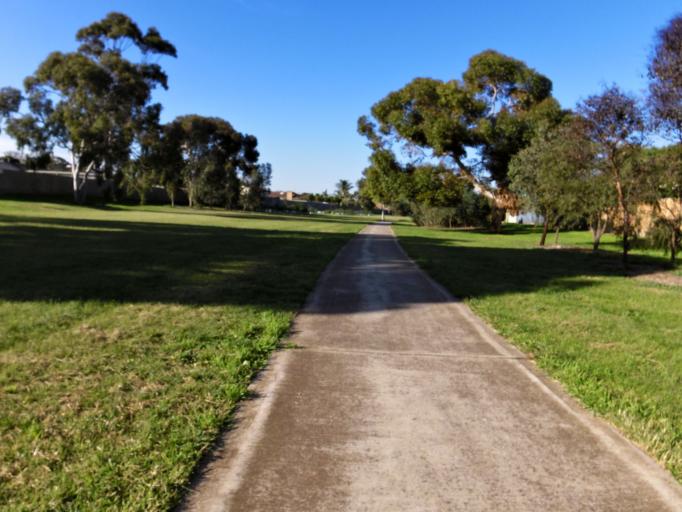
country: AU
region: Victoria
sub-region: Wyndham
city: Hoppers Crossing
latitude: -37.8694
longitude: 144.6996
